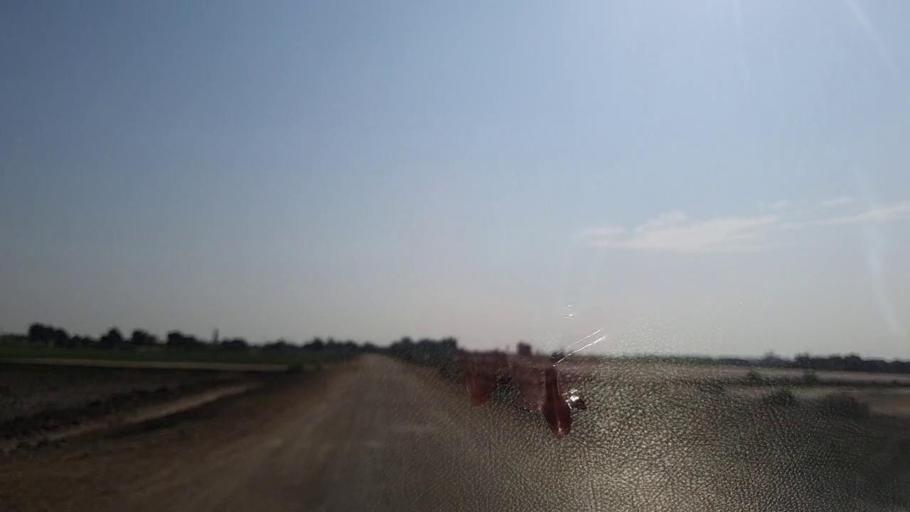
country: PK
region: Sindh
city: Tando Mittha Khan
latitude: 26.0317
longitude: 69.1150
